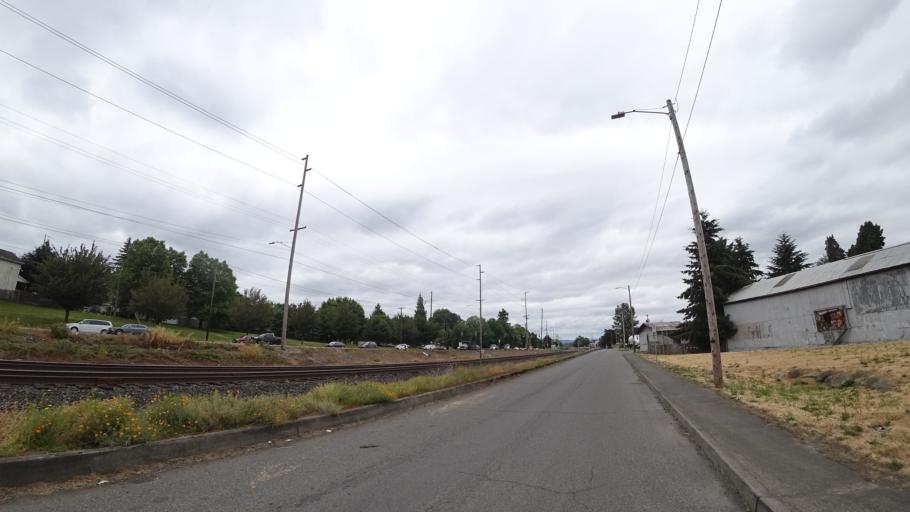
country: US
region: Washington
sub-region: Clark County
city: Vancouver
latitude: 45.5886
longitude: -122.6954
